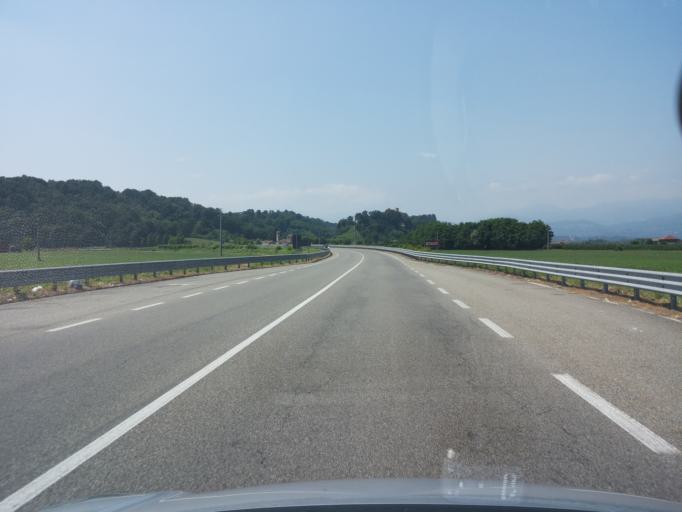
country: IT
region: Piedmont
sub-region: Provincia di Biella
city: Castelletto Cervo
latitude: 45.5250
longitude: 8.1988
